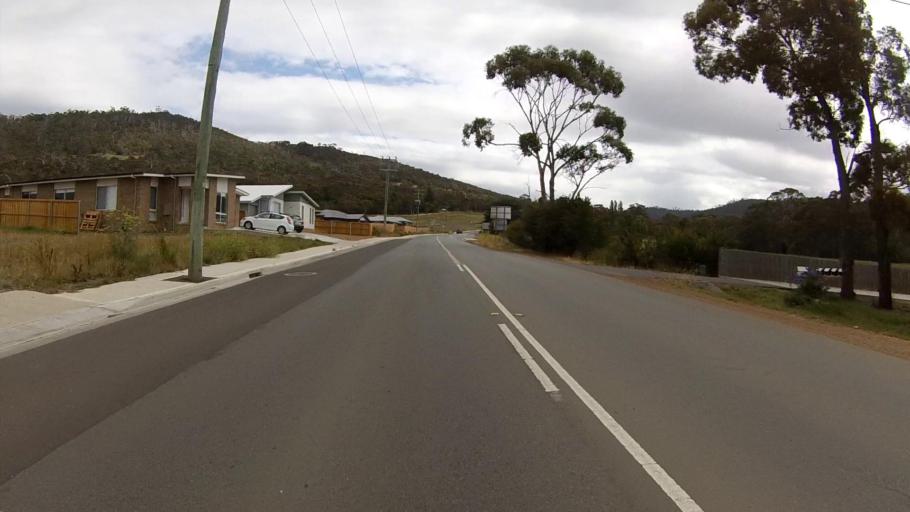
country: AU
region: Tasmania
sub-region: Clarence
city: Cambridge
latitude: -42.8373
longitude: 147.4398
